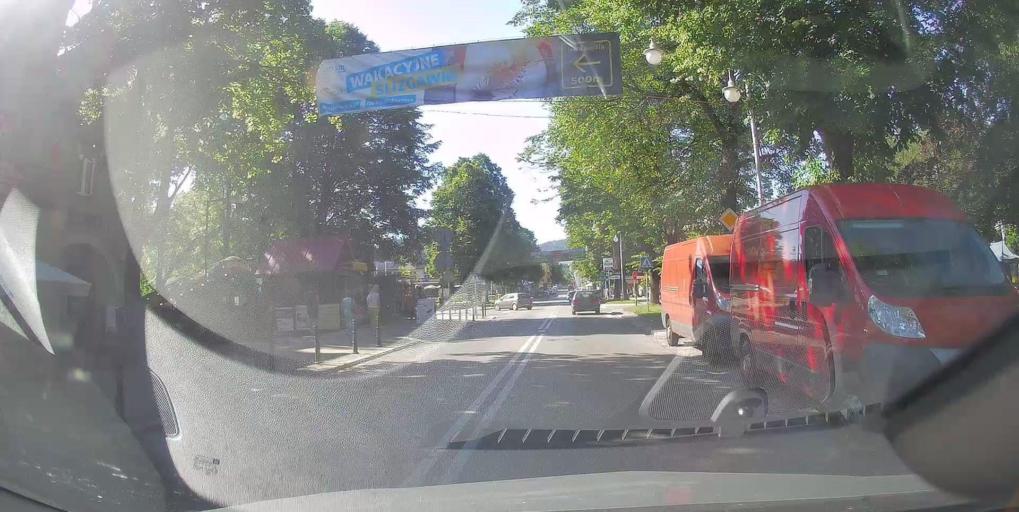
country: PL
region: Lesser Poland Voivodeship
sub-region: Powiat nowosadecki
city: Krynica-Zdroj
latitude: 49.4232
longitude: 20.9581
